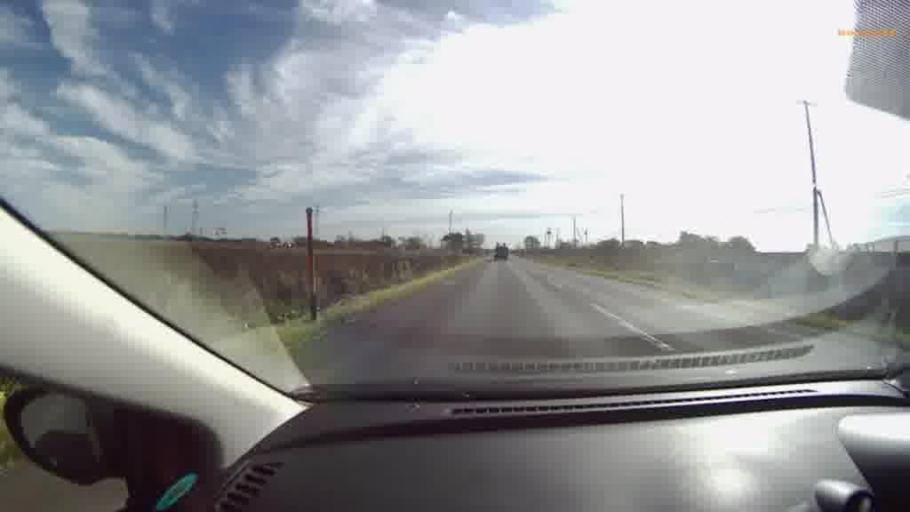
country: JP
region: Hokkaido
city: Kushiro
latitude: 43.0350
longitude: 144.2492
